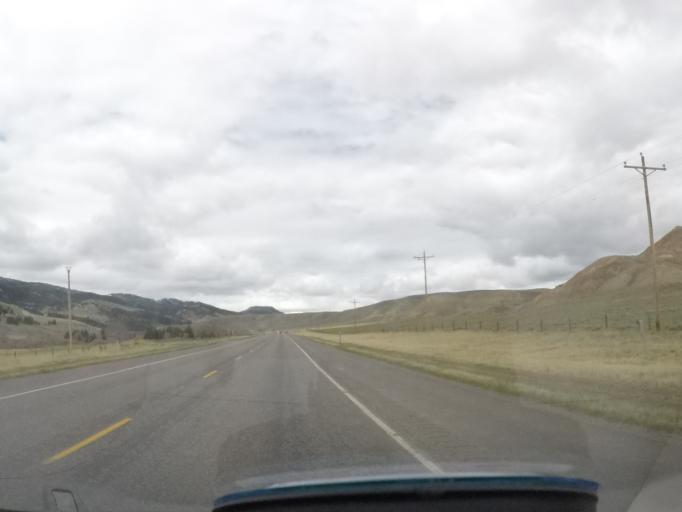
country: US
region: Wyoming
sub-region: Sublette County
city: Pinedale
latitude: 43.5742
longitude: -109.7292
